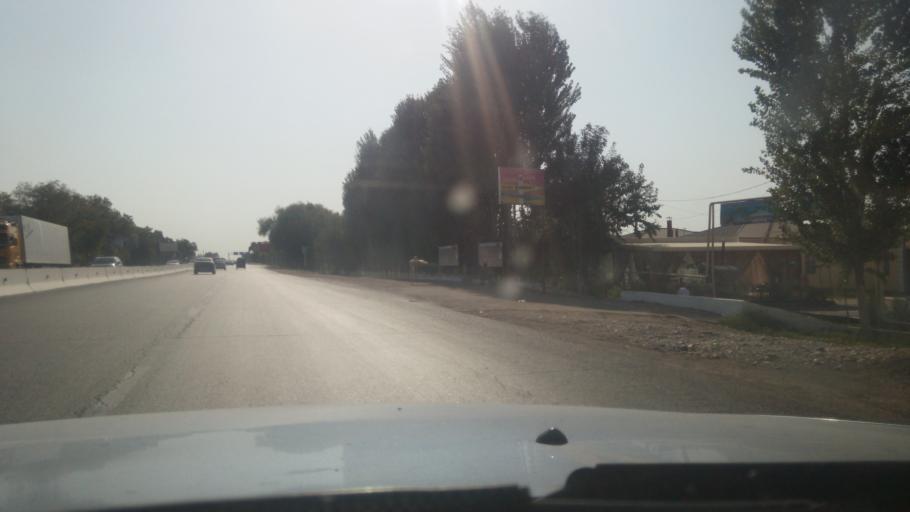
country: UZ
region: Toshkent
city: Urtaowul
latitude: 41.2258
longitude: 69.1442
